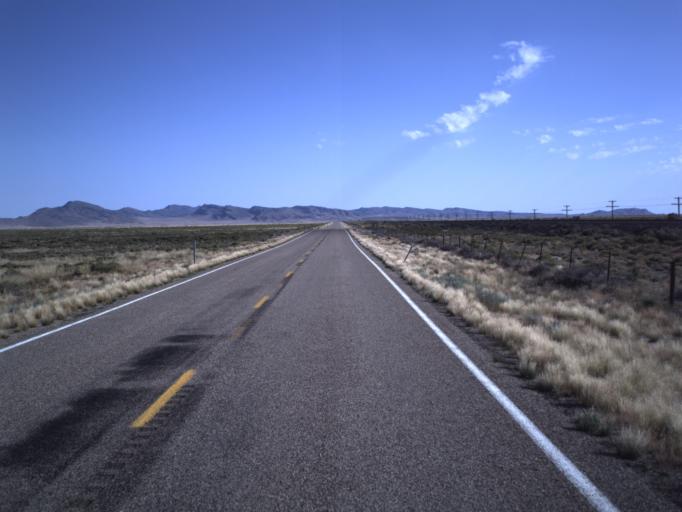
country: US
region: Utah
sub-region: Beaver County
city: Milford
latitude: 38.6381
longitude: -112.9835
